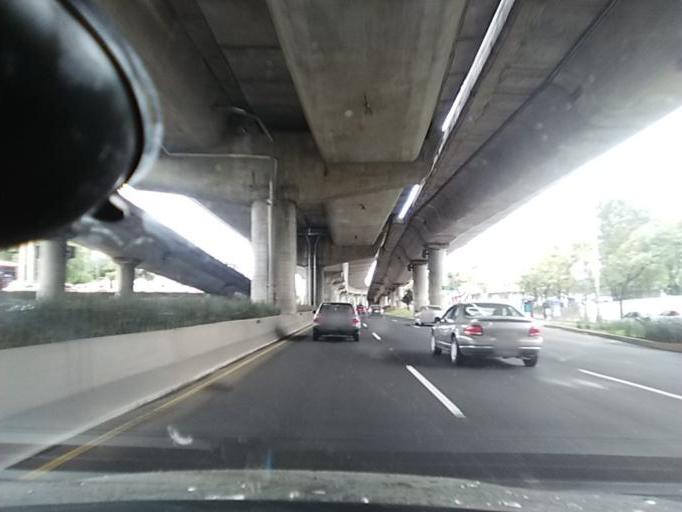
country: MX
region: Mexico City
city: Magdalena Contreras
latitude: 19.3296
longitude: -99.2113
